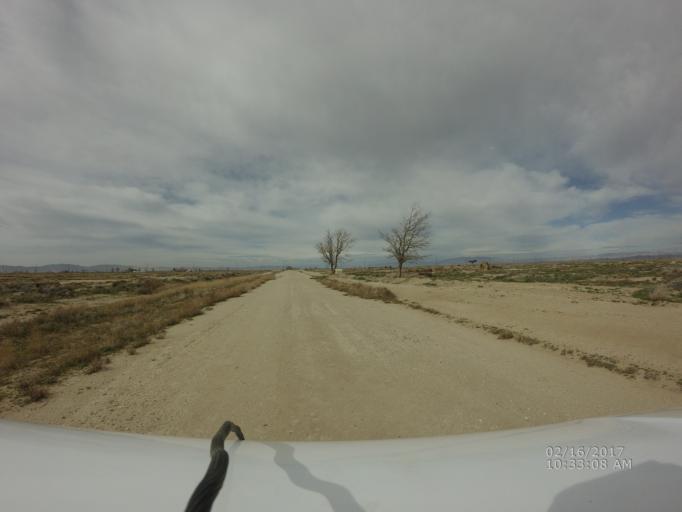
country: US
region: California
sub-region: Los Angeles County
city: Lancaster
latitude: 34.7269
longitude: -117.9635
